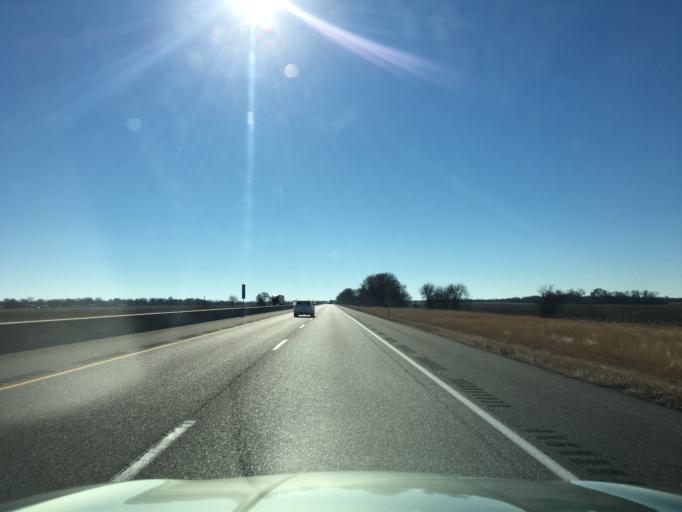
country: US
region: Kansas
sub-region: Sumner County
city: Belle Plaine
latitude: 37.4492
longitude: -97.3222
